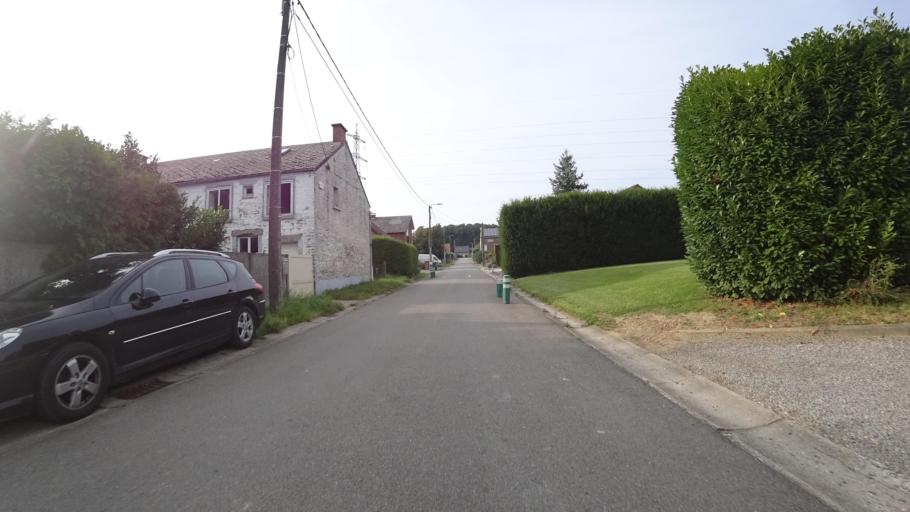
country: BE
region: Wallonia
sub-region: Province de Namur
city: Namur
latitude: 50.5218
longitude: 4.8372
